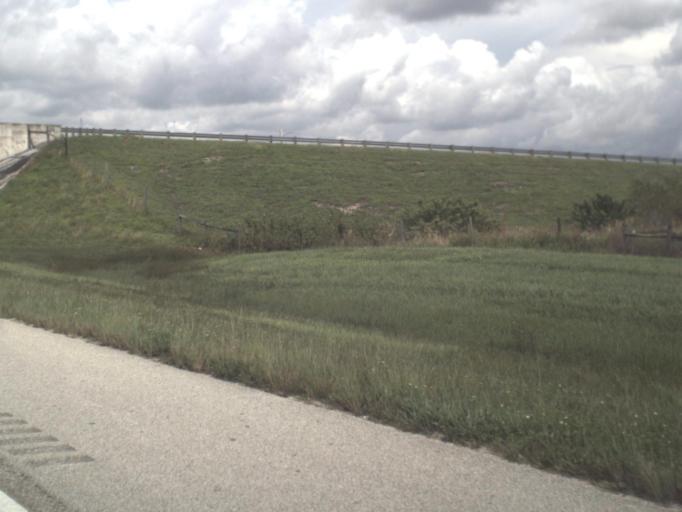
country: US
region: Florida
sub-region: Charlotte County
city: Punta Gorda
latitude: 26.9168
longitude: -82.0120
